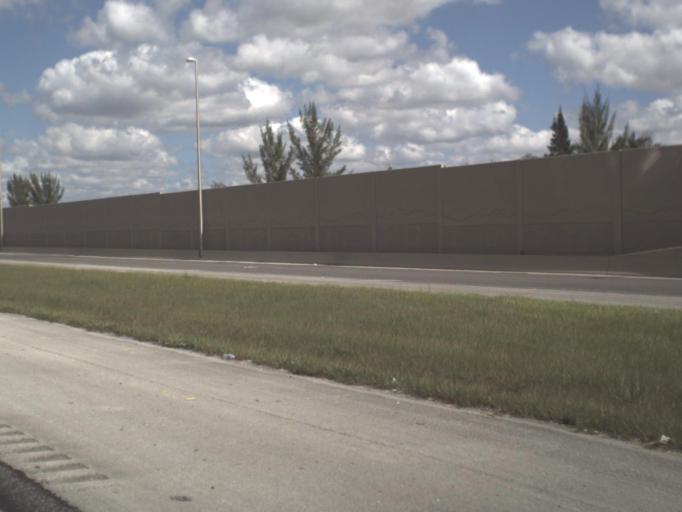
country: US
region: Florida
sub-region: Miami-Dade County
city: Doral
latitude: 25.8471
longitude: -80.3872
